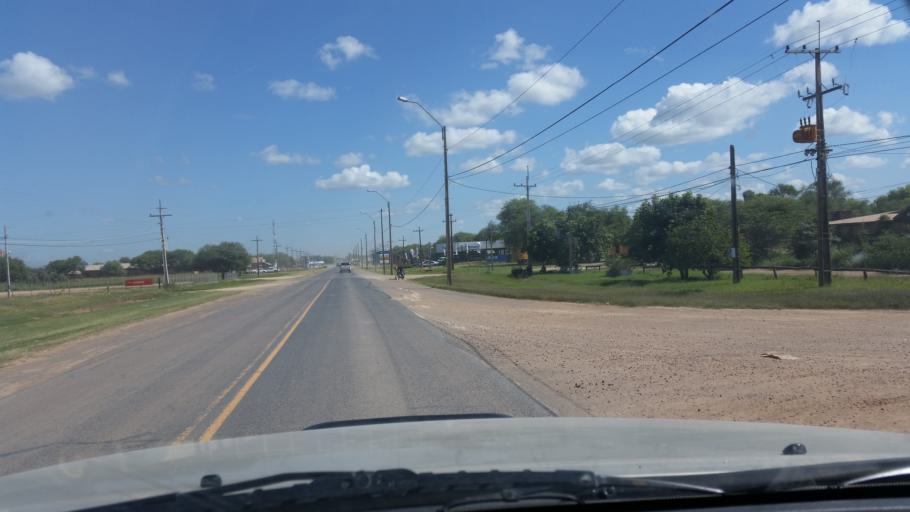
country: PY
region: Boqueron
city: Colonia Menno
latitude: -22.3942
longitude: -59.8364
